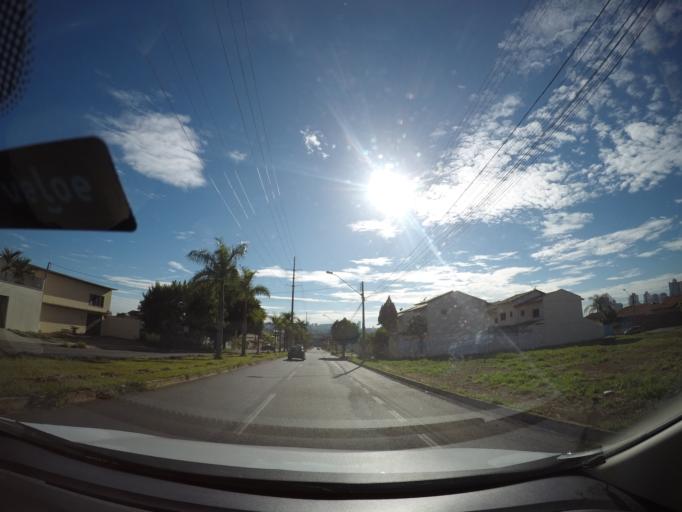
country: BR
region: Goias
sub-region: Goiania
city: Goiania
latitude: -16.7257
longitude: -49.2996
